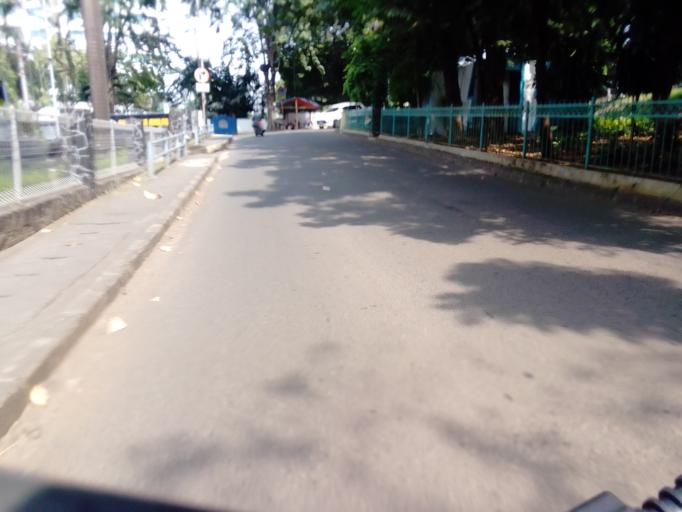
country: ID
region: Jakarta Raya
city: Jakarta
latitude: -6.2126
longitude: 106.8083
